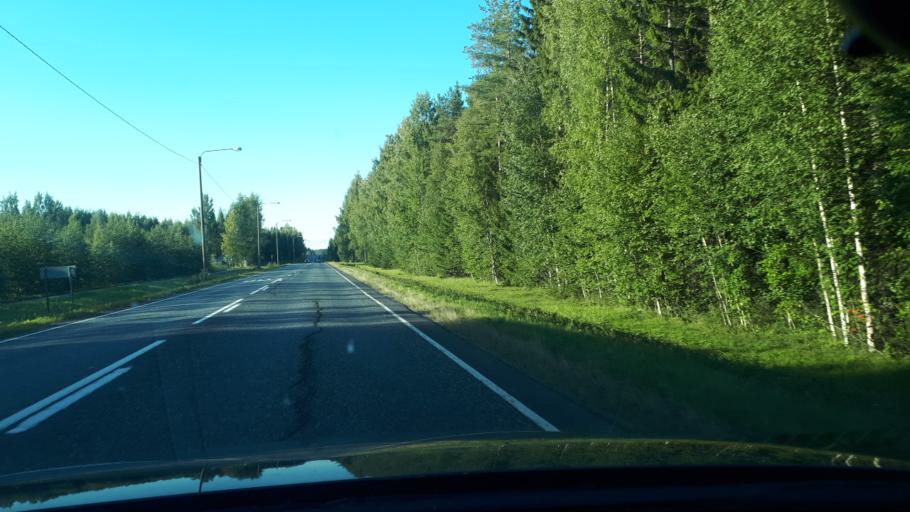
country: FI
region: Northern Savo
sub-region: Ylae-Savo
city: Lapinlahti
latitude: 63.4268
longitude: 27.3292
